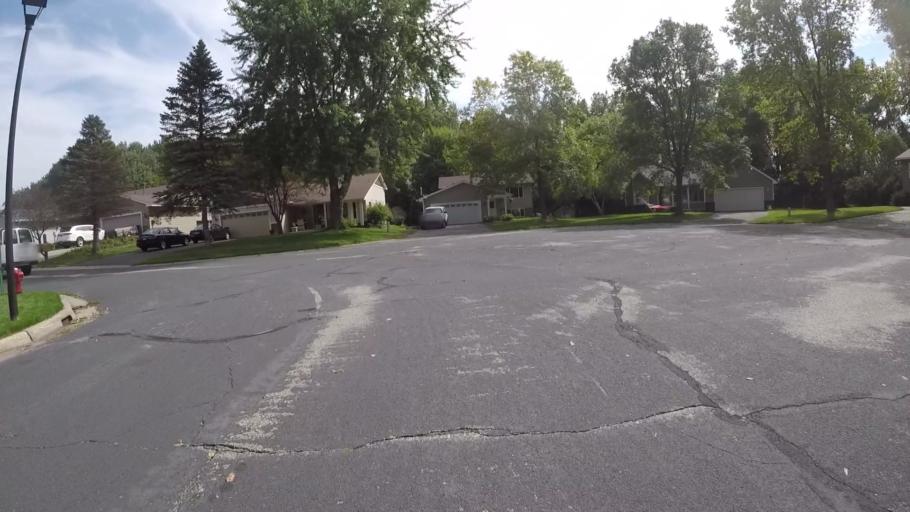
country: US
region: Minnesota
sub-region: Hennepin County
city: Eden Prairie
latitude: 44.8712
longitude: -93.4491
